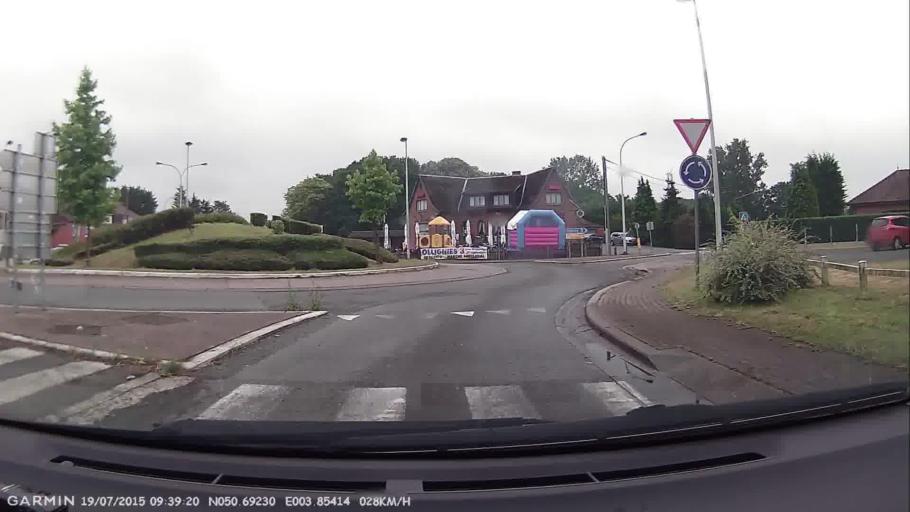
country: BE
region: Wallonia
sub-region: Province du Hainaut
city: Lessines
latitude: 50.6922
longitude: 3.8542
